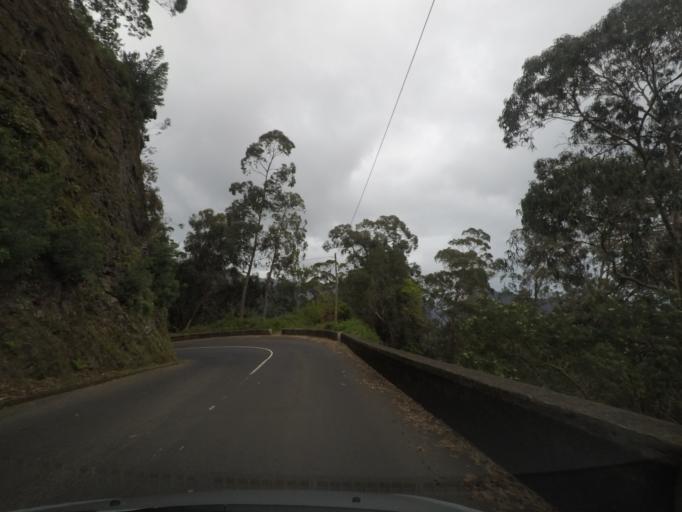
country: PT
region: Madeira
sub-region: Santa Cruz
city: Camacha
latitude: 32.7479
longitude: -16.8296
